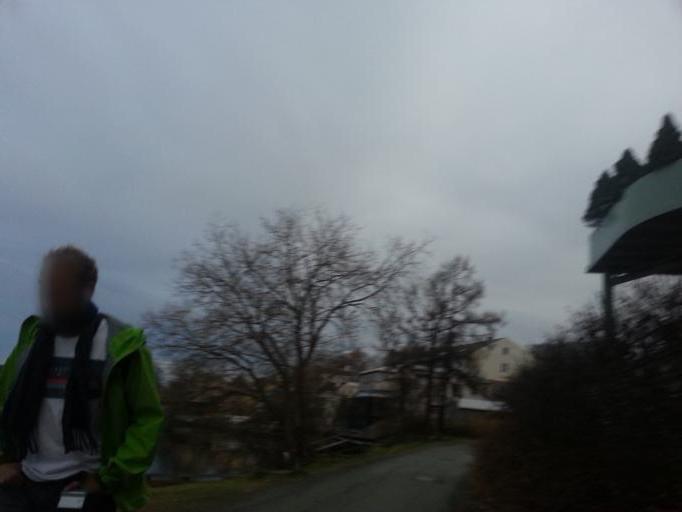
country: NO
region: Sor-Trondelag
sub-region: Trondheim
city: Trondheim
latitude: 63.4250
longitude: 10.4021
